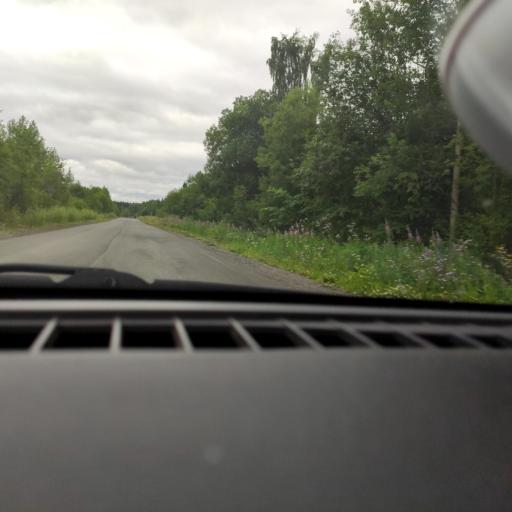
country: RU
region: Perm
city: Polazna
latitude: 58.3355
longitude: 56.1638
